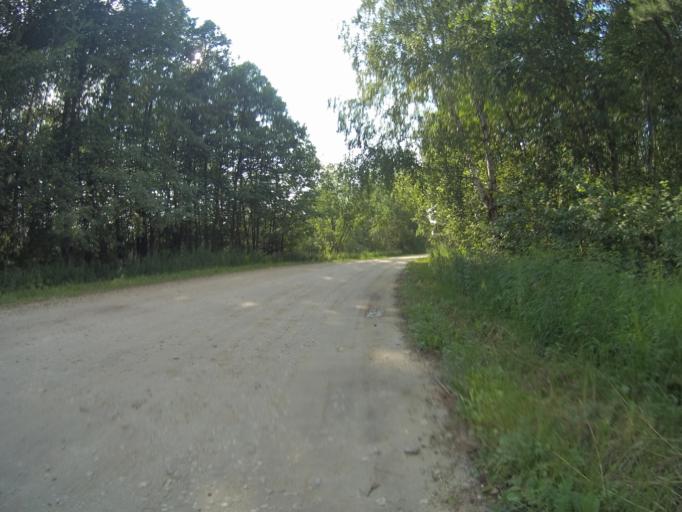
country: RU
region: Vladimir
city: Orgtrud
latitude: 56.3184
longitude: 40.7373
